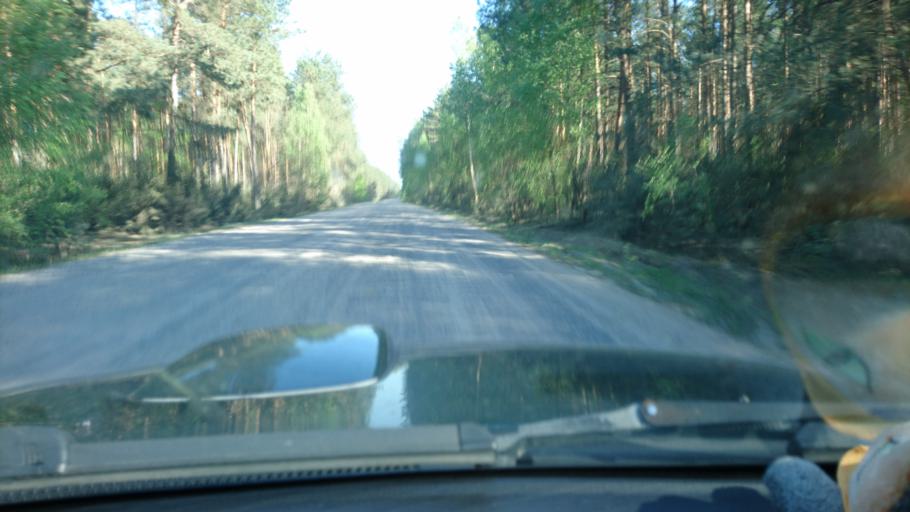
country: BY
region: Brest
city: Zhabinka
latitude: 52.3846
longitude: 24.1125
